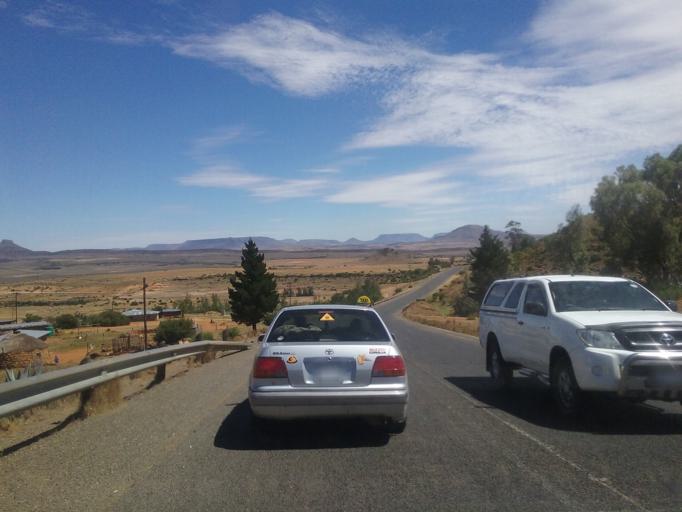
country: LS
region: Mohale's Hoek District
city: Mohale's Hoek
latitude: -30.1991
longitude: 27.4164
